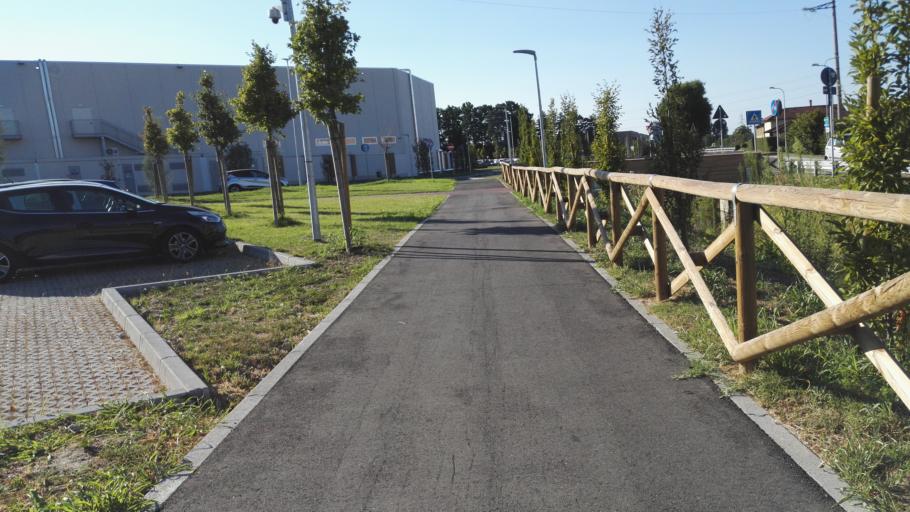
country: IT
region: Lombardy
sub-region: Citta metropolitana di Milano
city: Locate di Triulzi
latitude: 45.3603
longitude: 9.2196
